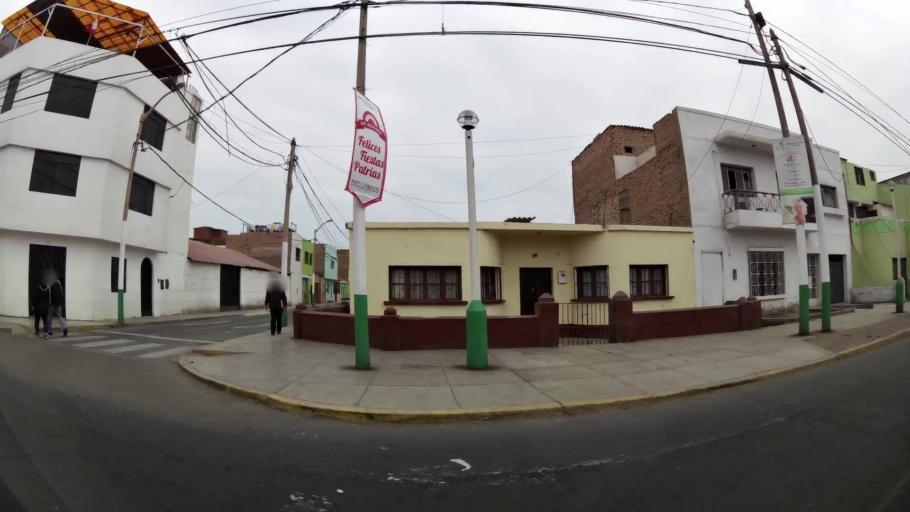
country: PE
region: Callao
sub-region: Callao
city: Callao
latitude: -12.0667
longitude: -77.1268
